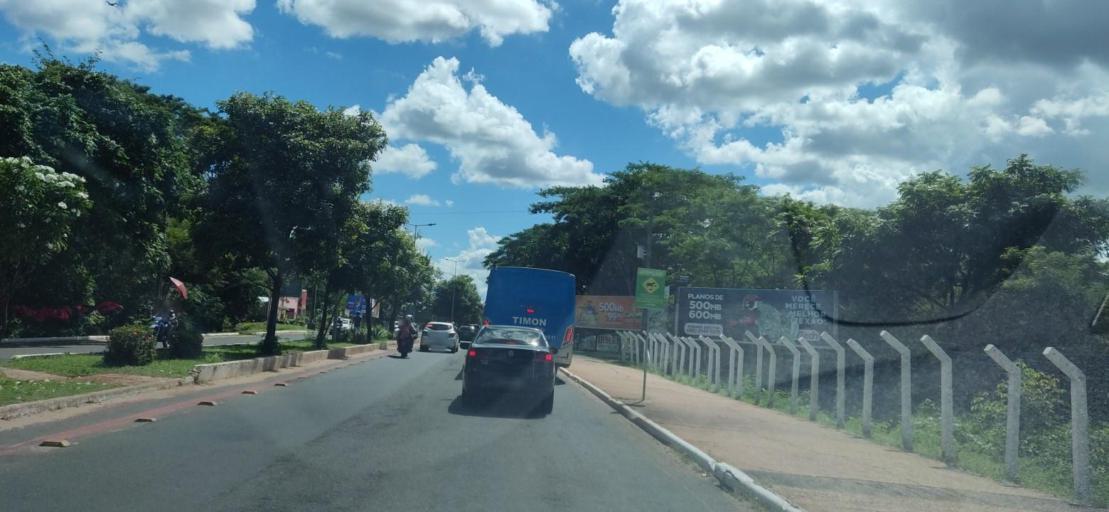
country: BR
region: Maranhao
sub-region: Timon
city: Timon
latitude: -5.0898
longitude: -42.8246
